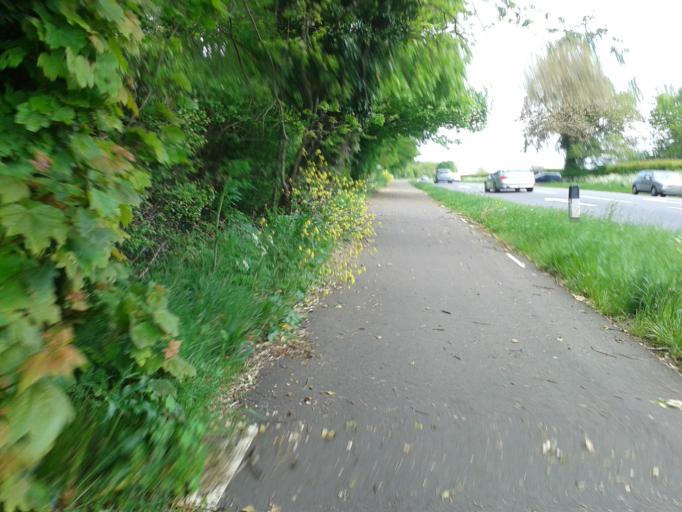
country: GB
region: England
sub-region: Cambridgeshire
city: Meldreth
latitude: 52.1073
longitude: 0.0422
